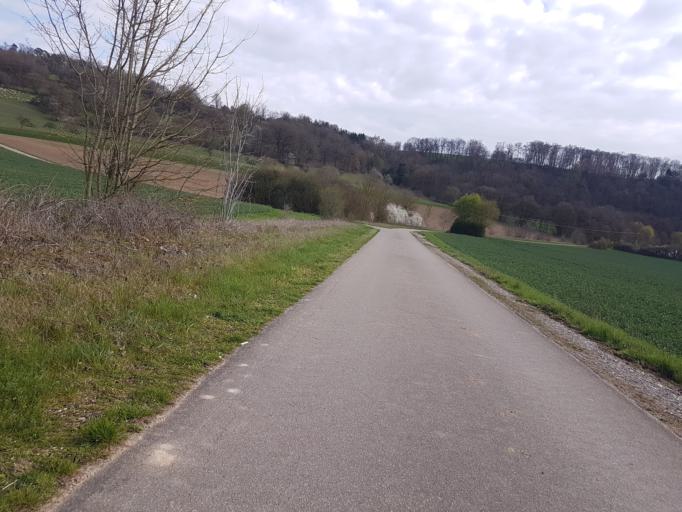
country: DE
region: Baden-Wuerttemberg
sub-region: Regierungsbezirk Stuttgart
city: Jagsthausen
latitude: 49.3382
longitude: 9.5147
